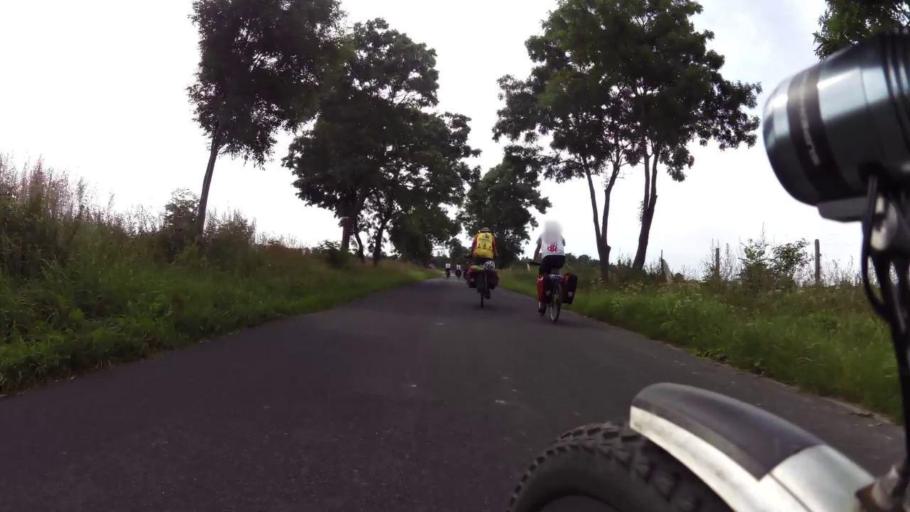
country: PL
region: West Pomeranian Voivodeship
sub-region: Powiat mysliborski
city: Debno
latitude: 52.7883
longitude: 14.6480
